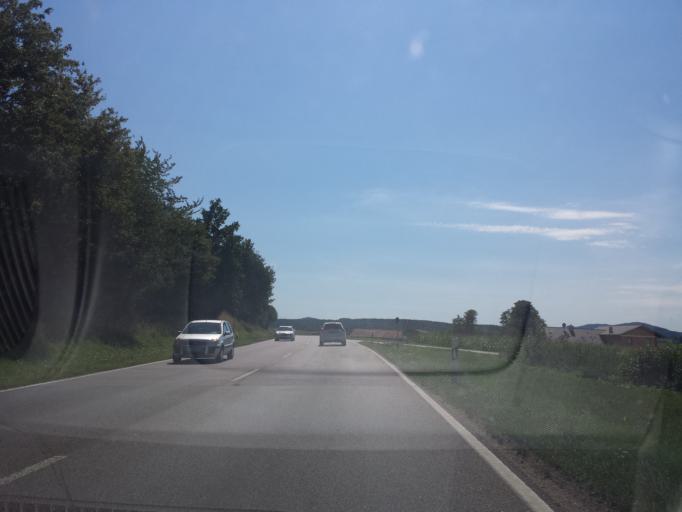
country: DE
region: Bavaria
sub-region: Upper Palatinate
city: Cham
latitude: 49.1954
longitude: 12.6558
